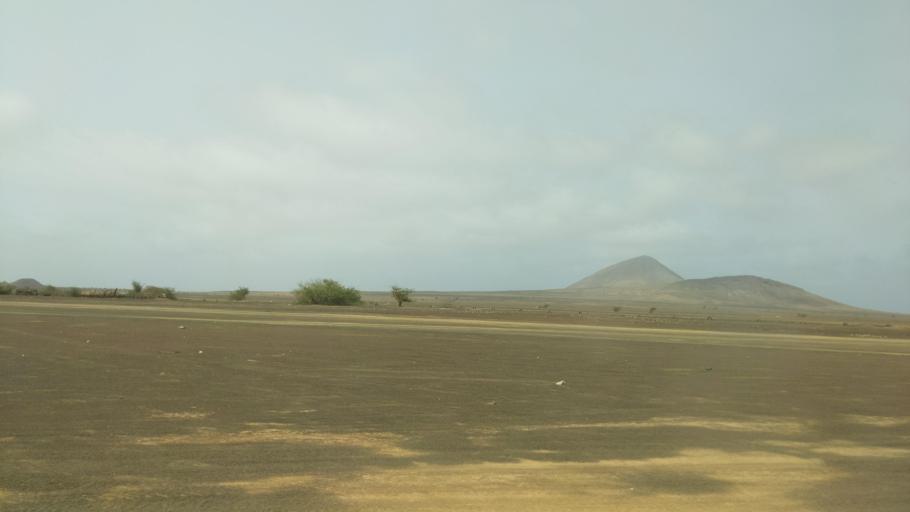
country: CV
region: Sal
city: Espargos
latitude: 16.7956
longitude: -22.9529
